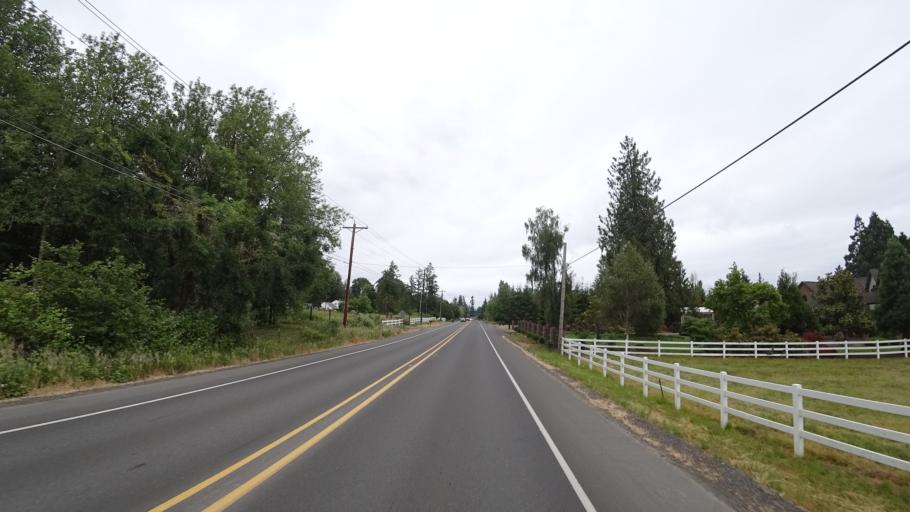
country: US
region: Oregon
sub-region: Washington County
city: Aloha
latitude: 45.4778
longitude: -122.9326
